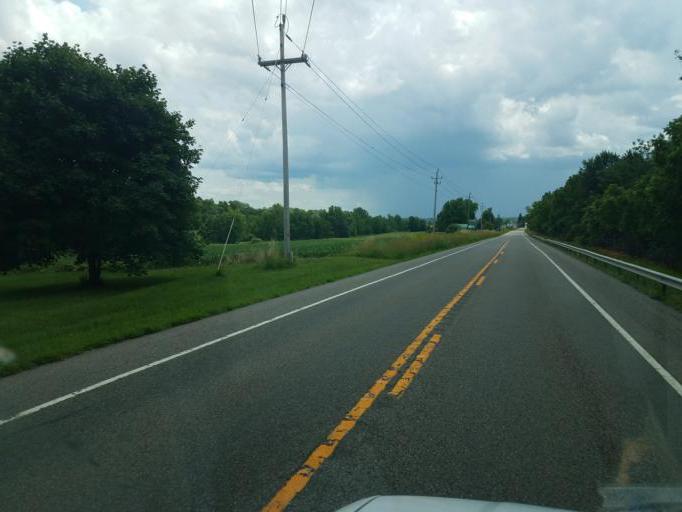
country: US
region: New York
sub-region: Wayne County
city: Clyde
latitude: 43.0022
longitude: -76.8545
